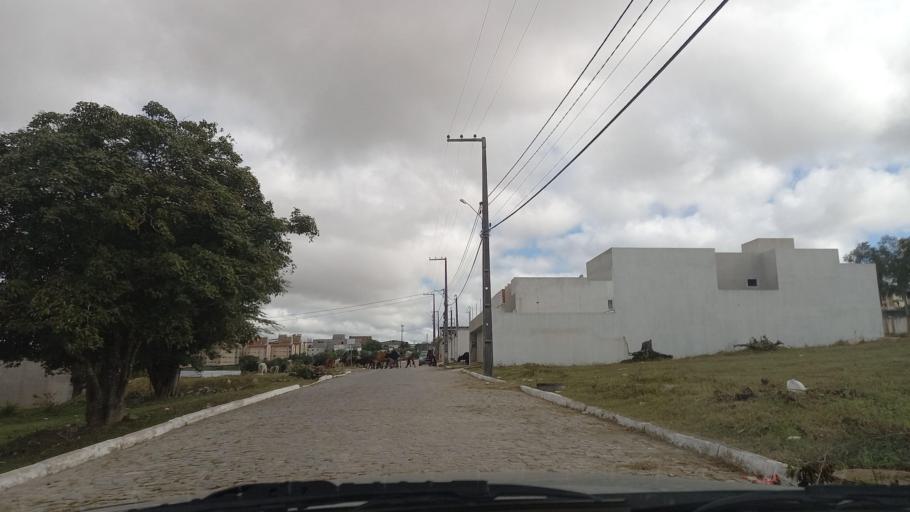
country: BR
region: Pernambuco
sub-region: Caruaru
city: Caruaru
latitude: -8.3040
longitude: -35.9550
